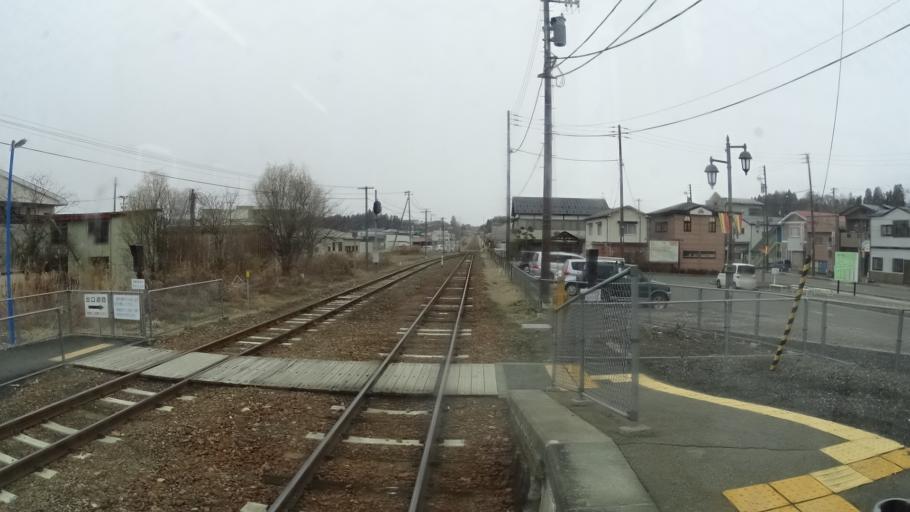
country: JP
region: Iwate
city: Hanamaki
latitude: 39.3838
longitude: 141.2319
